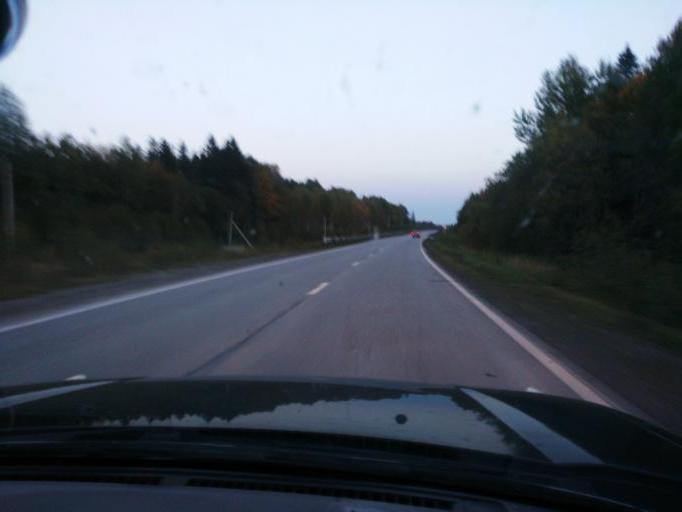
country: RU
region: Perm
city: Verkhnechusovskiye Gorodki
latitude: 58.2561
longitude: 56.9992
